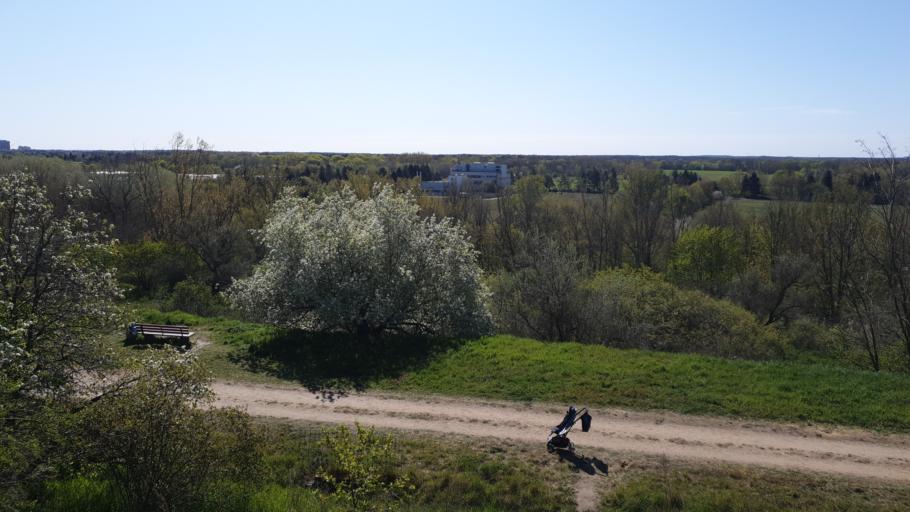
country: DE
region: Berlin
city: Marienfelde
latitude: 52.4000
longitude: 13.3702
